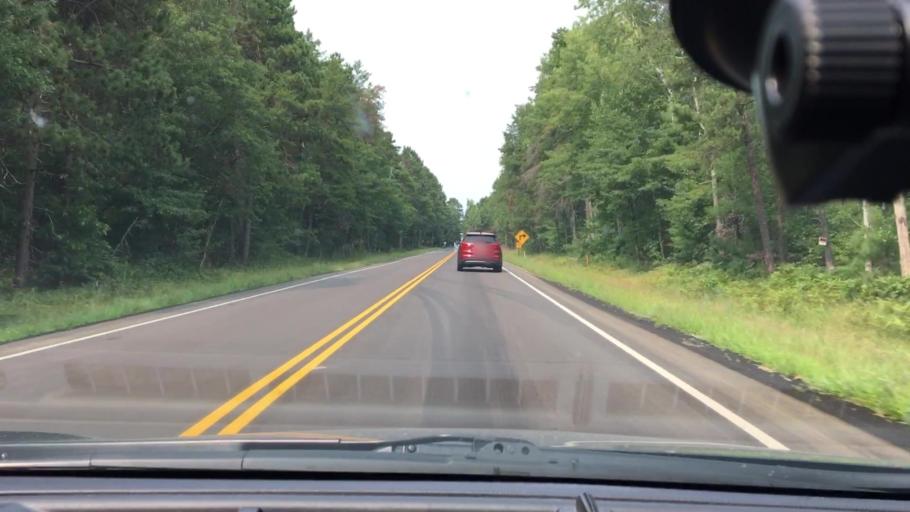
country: US
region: Minnesota
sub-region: Crow Wing County
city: Breezy Point
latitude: 46.5310
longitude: -94.1823
